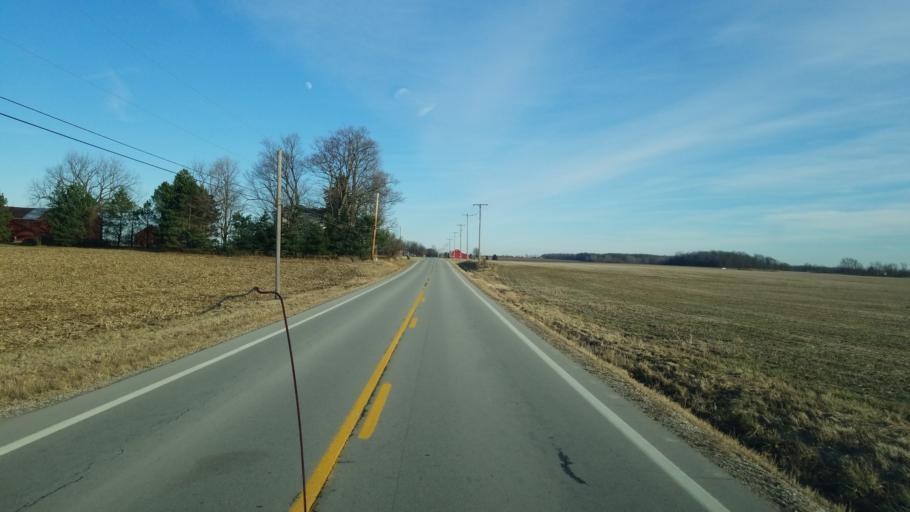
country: US
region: Ohio
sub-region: Huron County
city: Greenwich
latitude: 41.1039
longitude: -82.5978
